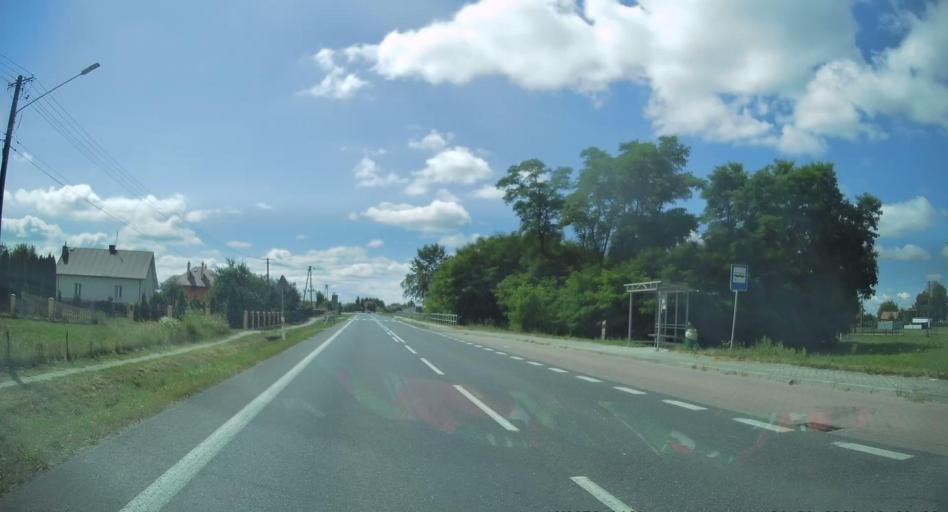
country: PL
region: Subcarpathian Voivodeship
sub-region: Powiat mielecki
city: Przeclaw
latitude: 50.1557
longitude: 21.4843
